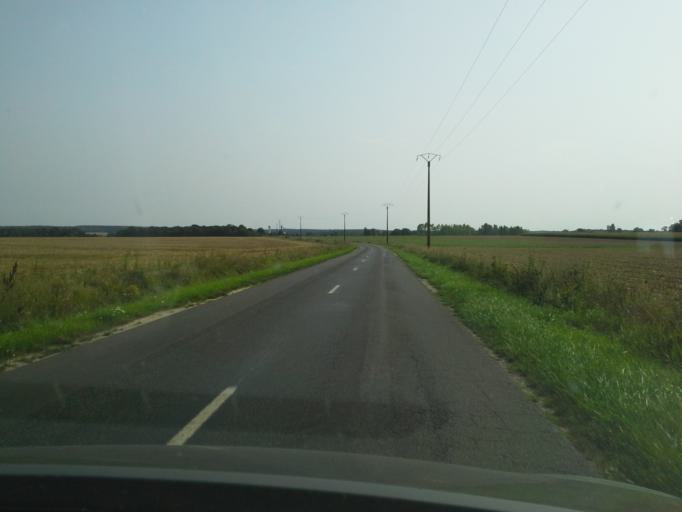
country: FR
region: Centre
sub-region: Departement du Loir-et-Cher
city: La Ville-aux-Clercs
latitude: 47.9106
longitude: 1.0675
